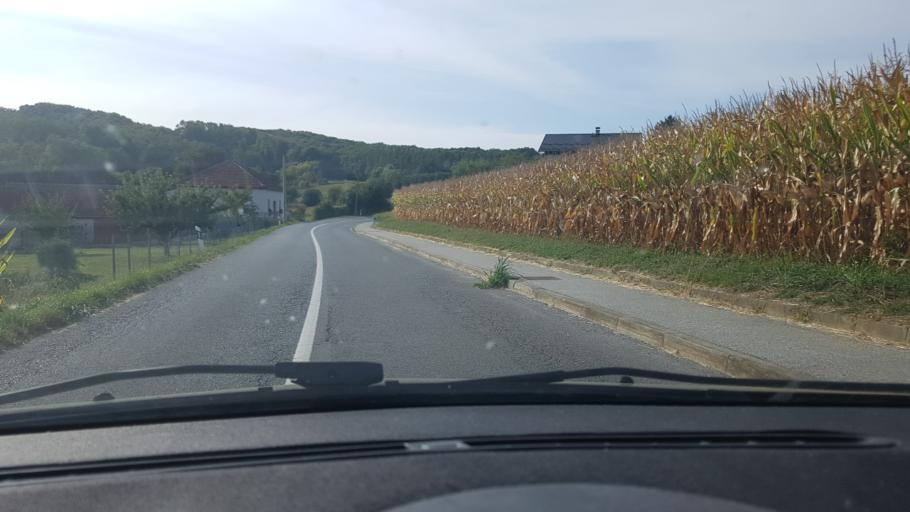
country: HR
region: Krapinsko-Zagorska
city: Mihovljan
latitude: 46.1285
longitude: 15.9731
